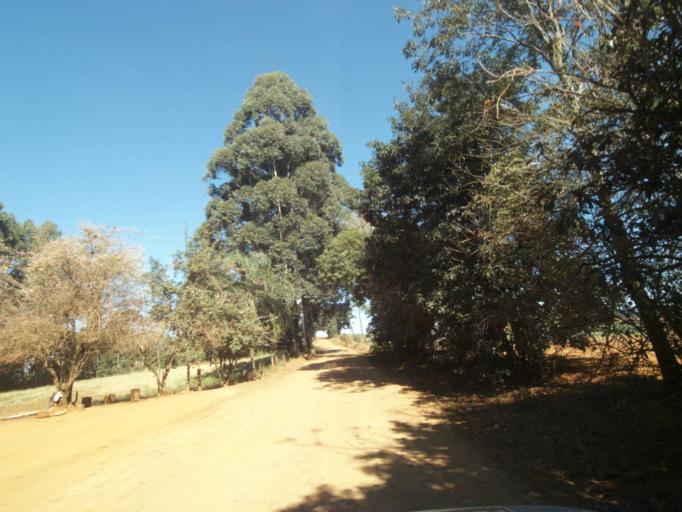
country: BR
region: Parana
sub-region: Tibagi
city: Tibagi
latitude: -24.5565
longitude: -50.6215
